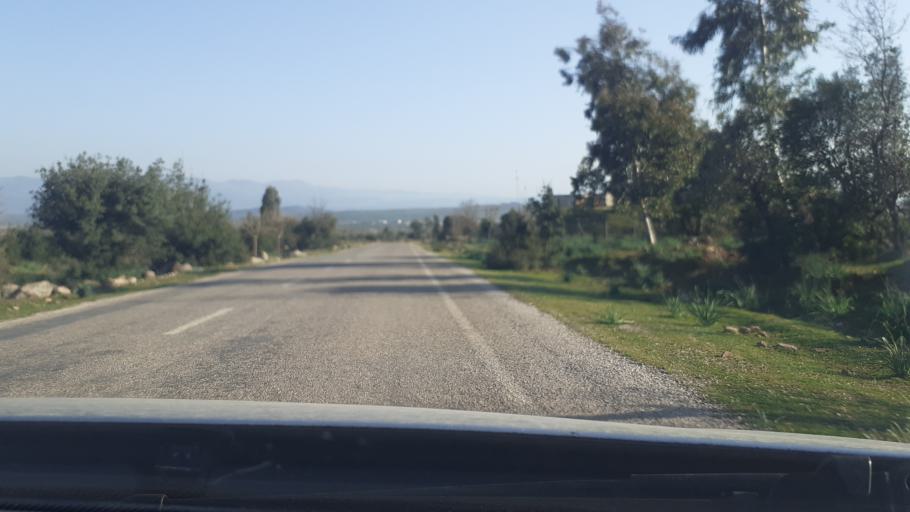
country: TR
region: Hatay
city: Aktepe
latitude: 36.7270
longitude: 36.4837
